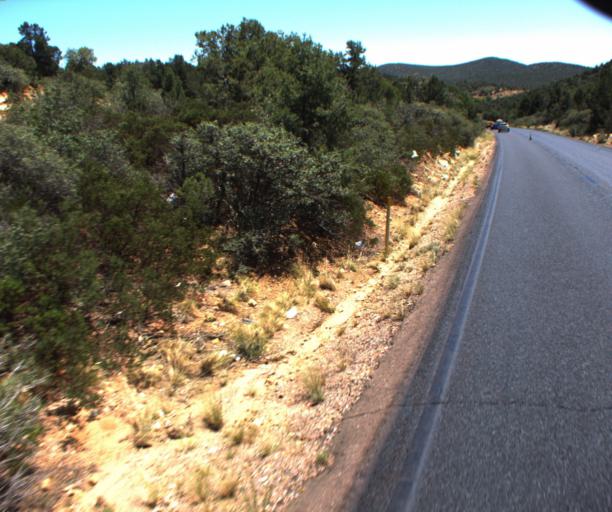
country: US
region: Arizona
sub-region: Gila County
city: Payson
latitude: 34.2023
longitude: -111.3313
